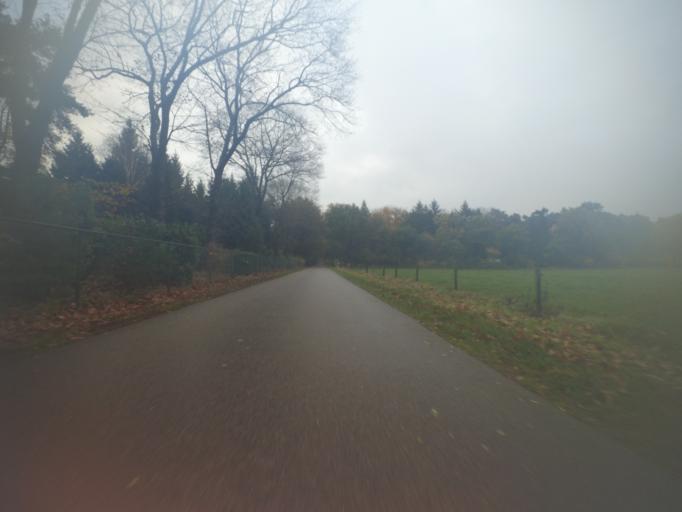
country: NL
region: Gelderland
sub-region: Gemeente Ede
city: Lunteren
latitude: 52.1059
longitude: 5.6487
